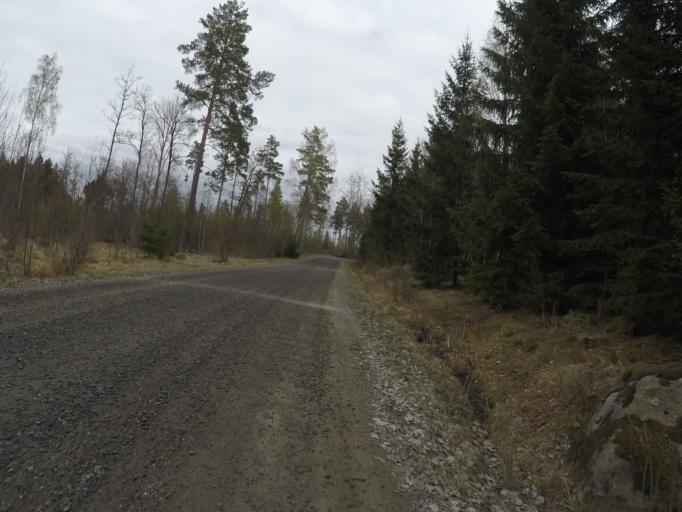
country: SE
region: Soedermanland
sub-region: Eskilstuna Kommun
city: Kvicksund
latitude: 59.3841
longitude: 16.3227
